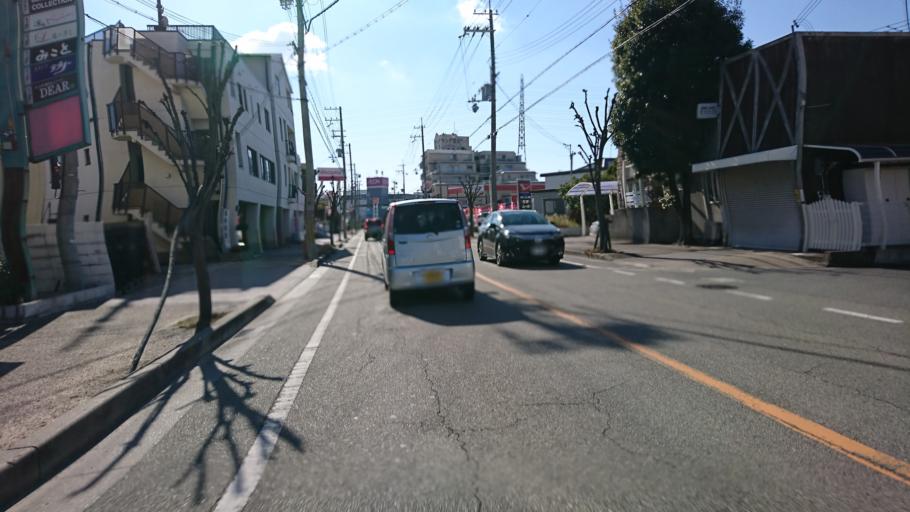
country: JP
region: Hyogo
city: Kakogawacho-honmachi
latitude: 34.7730
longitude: 134.8032
